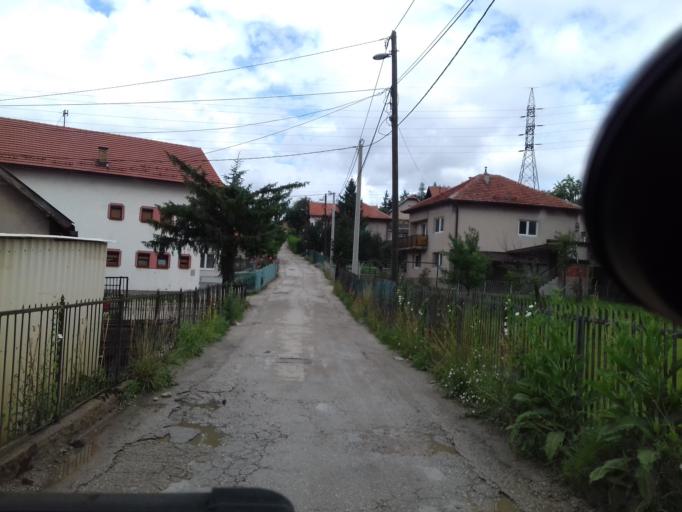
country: BA
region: Federation of Bosnia and Herzegovina
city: Zenica
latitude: 44.1985
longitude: 17.9297
